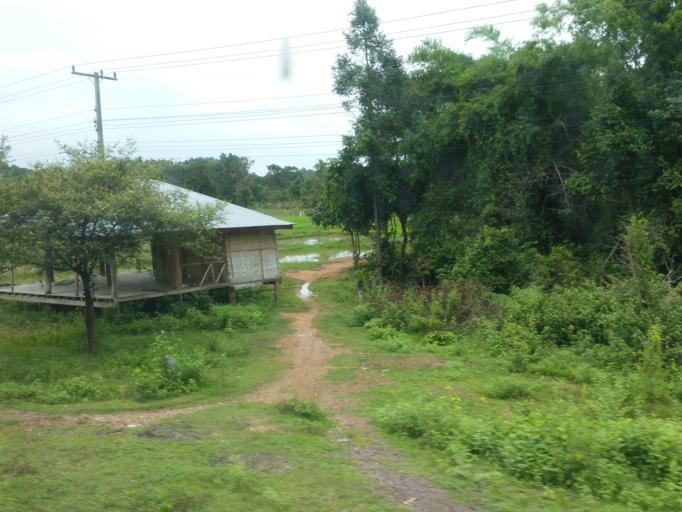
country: LA
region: Champasak
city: Khong
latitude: 14.1166
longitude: 105.8734
